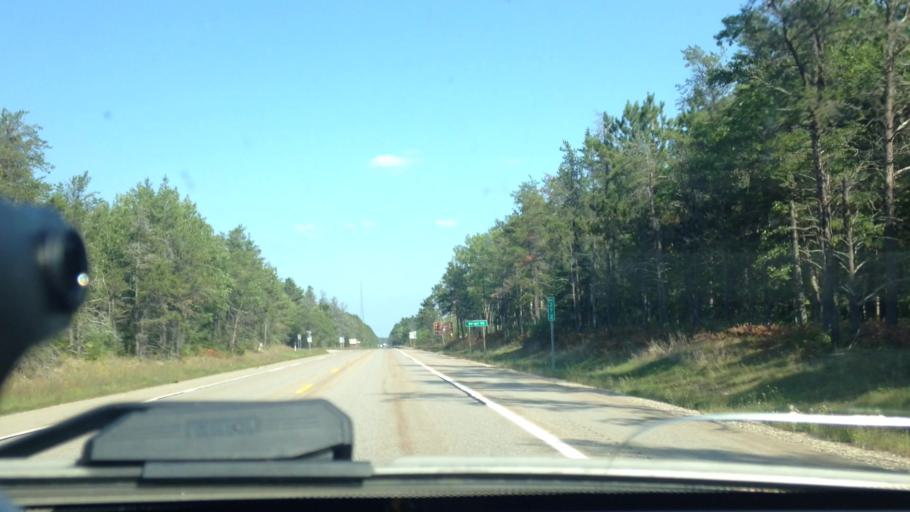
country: US
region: Michigan
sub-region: Chippewa County
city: Sault Ste. Marie
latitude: 46.3689
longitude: -84.7414
